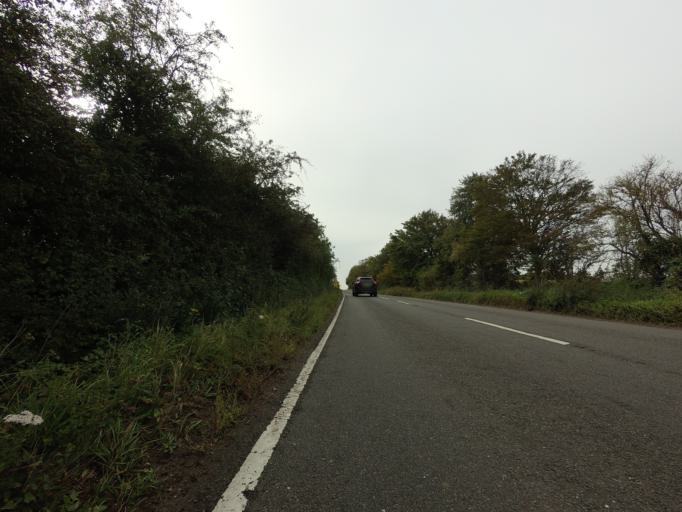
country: GB
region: England
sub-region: Cambridgeshire
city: Melbourn
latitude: 52.0345
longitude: 0.0411
